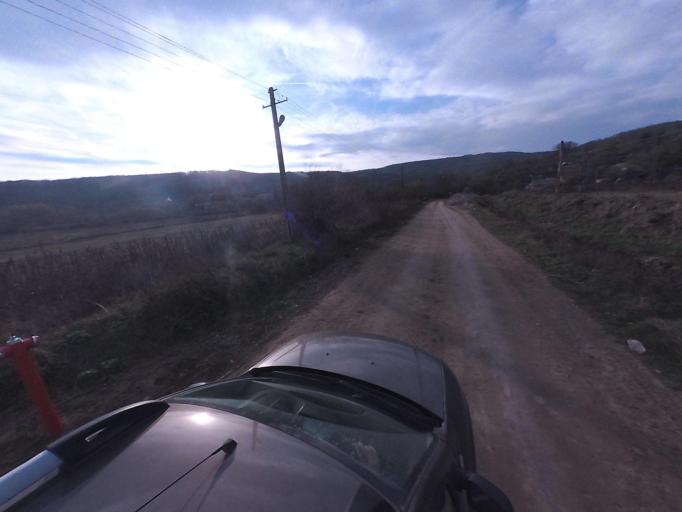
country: RO
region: Vaslui
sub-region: Comuna Gherghesti
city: Gherghesti
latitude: 46.4909
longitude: 27.5312
